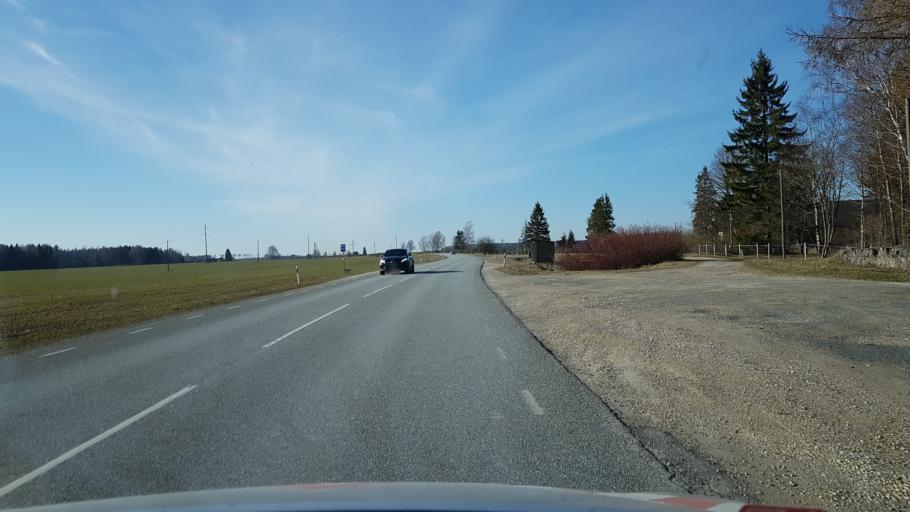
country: EE
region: Laeaene-Virumaa
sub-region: Vinni vald
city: Vinni
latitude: 59.2065
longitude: 26.5552
